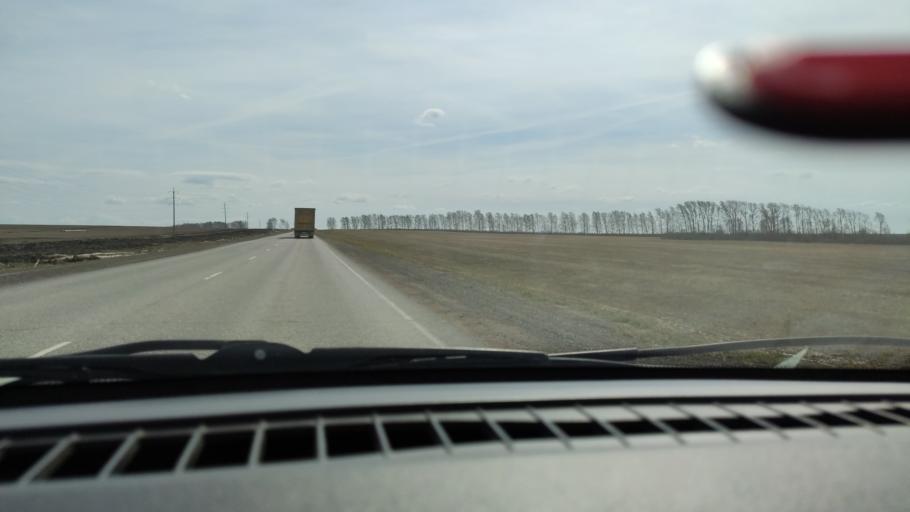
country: RU
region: Bashkortostan
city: Dyurtyuli
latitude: 55.3153
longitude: 54.9892
